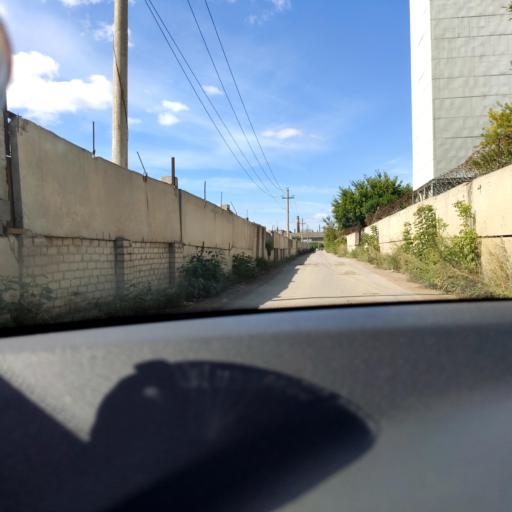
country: RU
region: Samara
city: Samara
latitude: 53.2004
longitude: 50.2708
